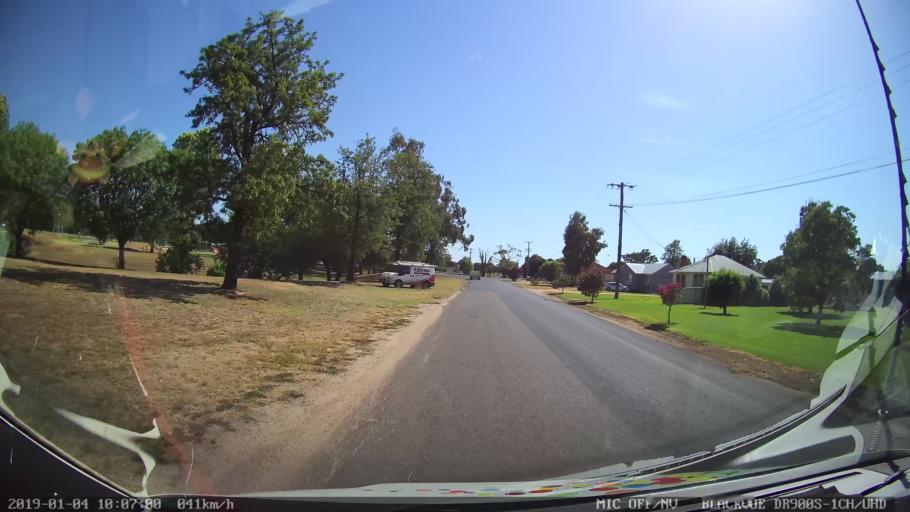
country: AU
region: New South Wales
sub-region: Cabonne
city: Canowindra
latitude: -33.4308
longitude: 148.3707
